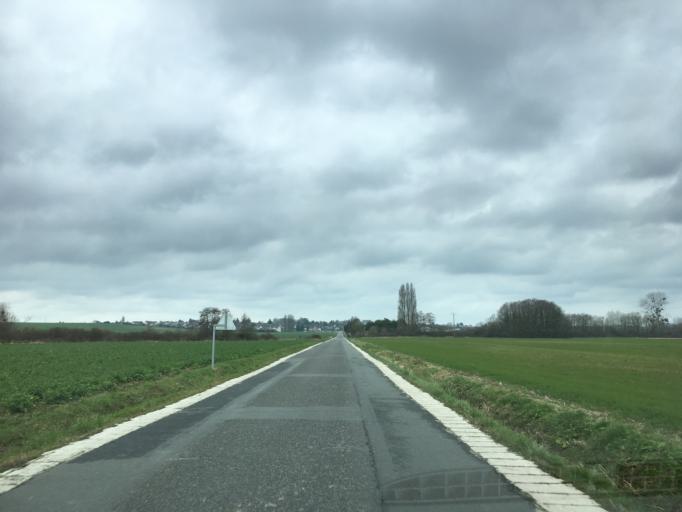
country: FR
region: Centre
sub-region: Departement d'Indre-et-Loire
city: Chanceaux-sur-Choisille
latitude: 47.4753
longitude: 0.7212
